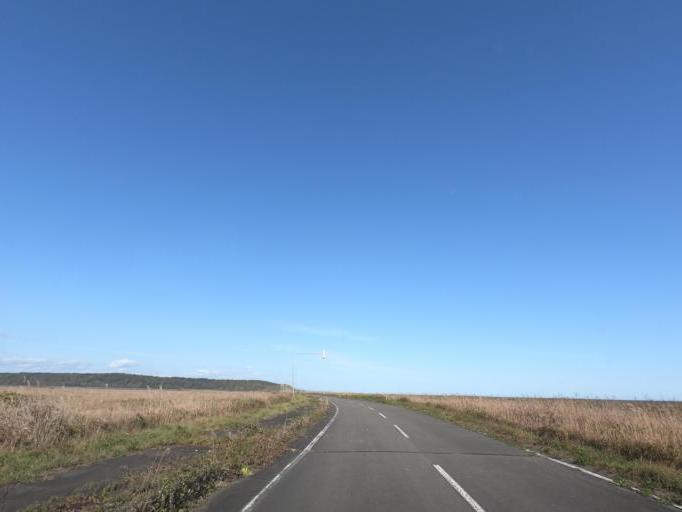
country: JP
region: Hokkaido
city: Obihiro
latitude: 42.5899
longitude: 143.5396
